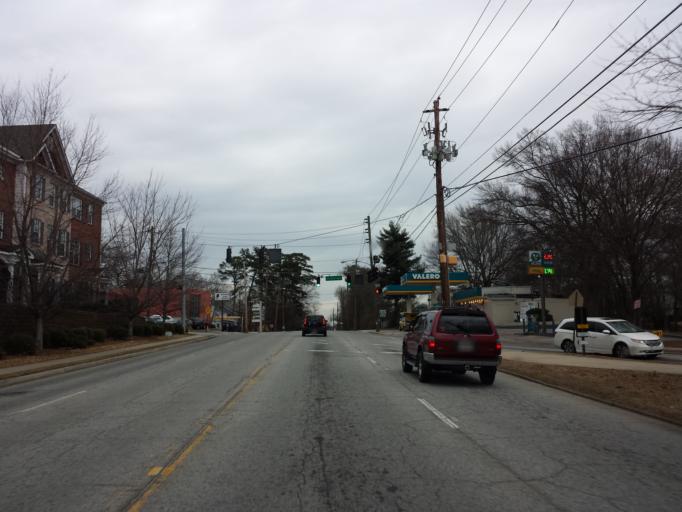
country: US
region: Georgia
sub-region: DeKalb County
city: Decatur
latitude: 33.7672
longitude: -84.3053
